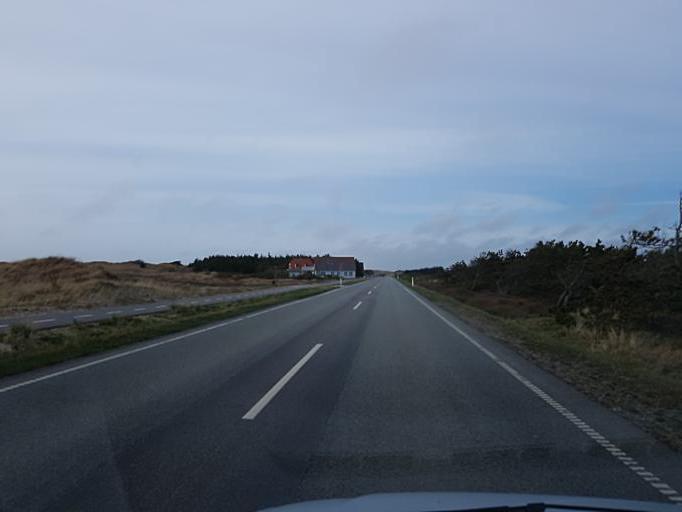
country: DK
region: Central Jutland
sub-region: Ringkobing-Skjern Kommune
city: Hvide Sande
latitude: 55.9315
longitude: 8.1608
